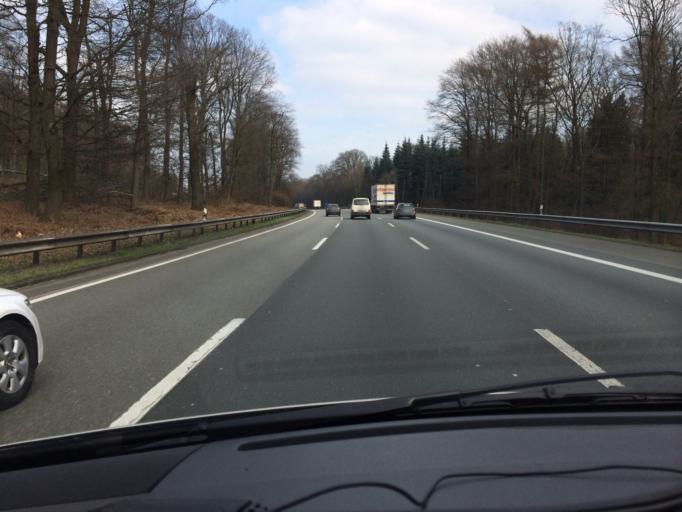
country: DE
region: North Rhine-Westphalia
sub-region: Regierungsbezirk Detmold
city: Bad Salzuflen
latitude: 52.1118
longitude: 8.7351
